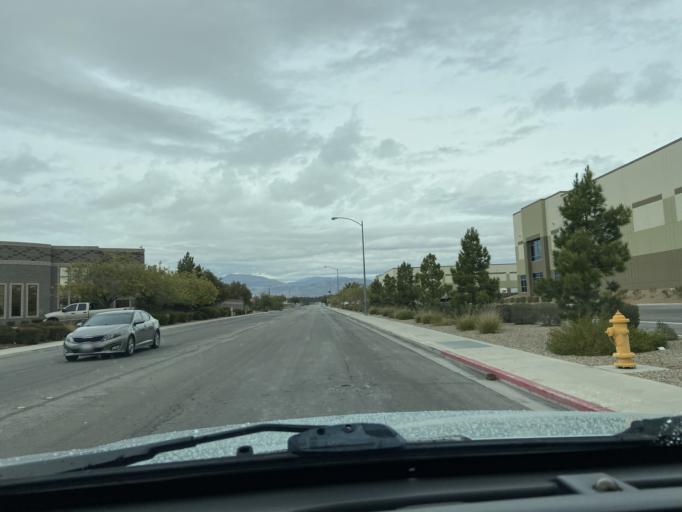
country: US
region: Nevada
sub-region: Clark County
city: North Las Vegas
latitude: 36.2442
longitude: -115.1123
